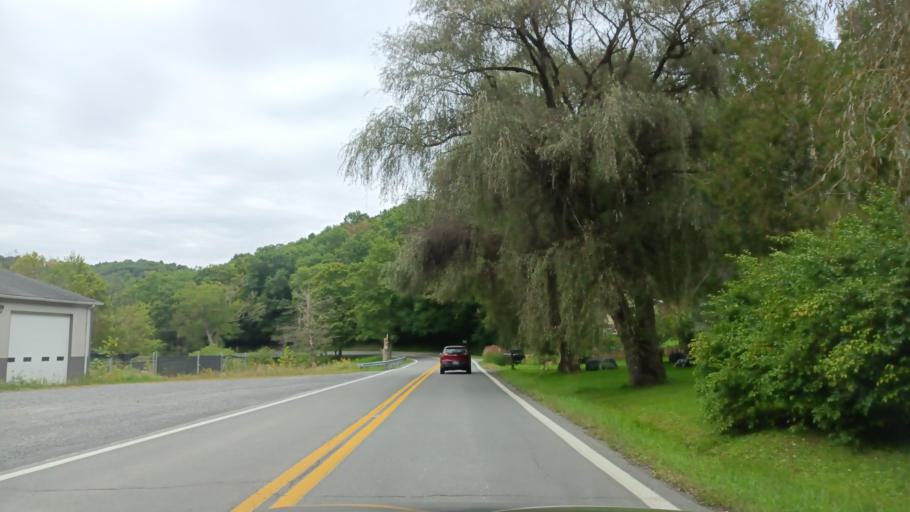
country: US
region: West Virginia
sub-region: Taylor County
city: Grafton
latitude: 39.3342
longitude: -79.8989
